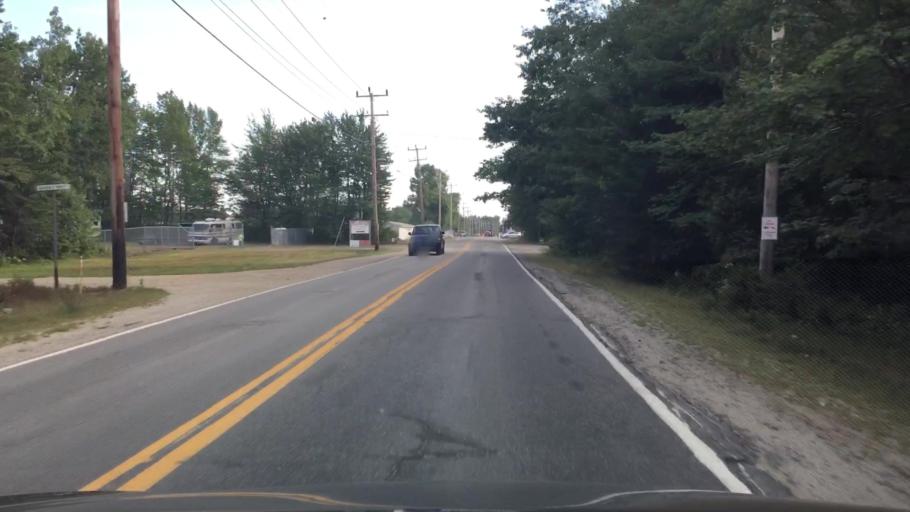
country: US
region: Maine
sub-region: Hancock County
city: Surry
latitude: 44.4327
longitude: -68.5741
